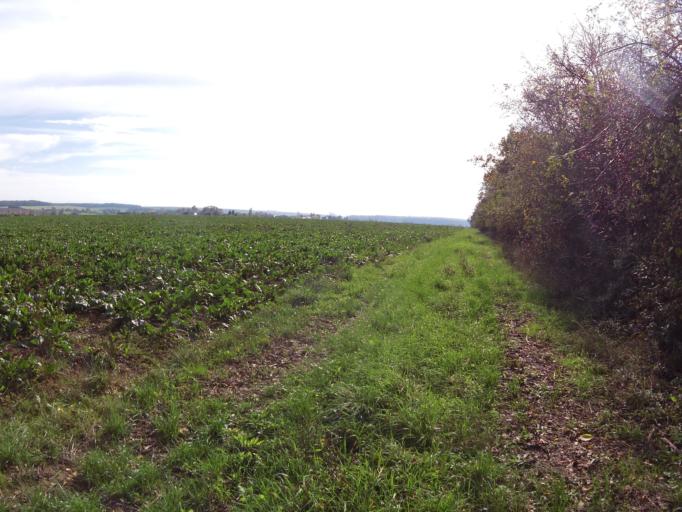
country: DE
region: Bavaria
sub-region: Regierungsbezirk Unterfranken
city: Frickenhausen
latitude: 49.7140
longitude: 10.0733
